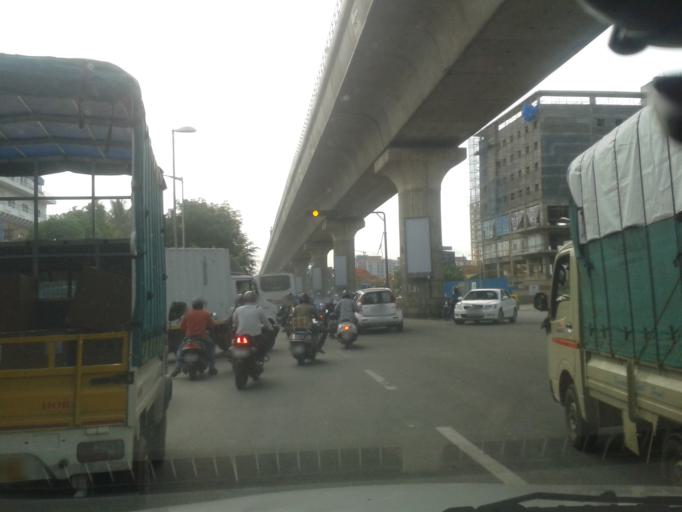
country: IN
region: Karnataka
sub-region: Bangalore Urban
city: Bangalore
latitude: 13.0239
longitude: 77.5485
